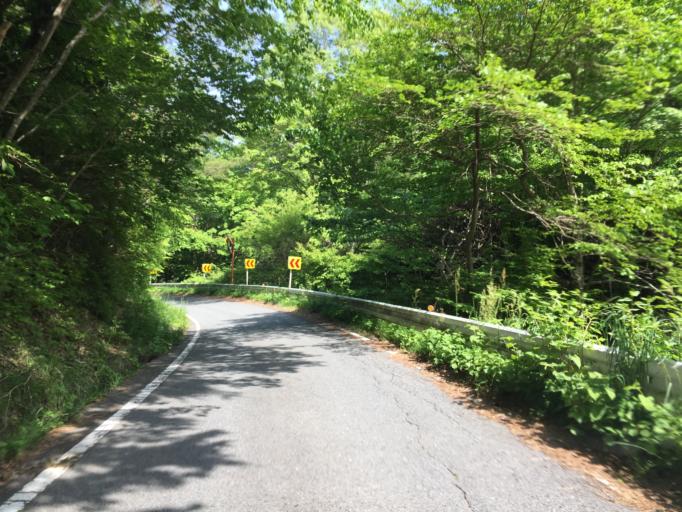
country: JP
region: Fukushima
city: Ishikawa
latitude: 37.0026
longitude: 140.5994
